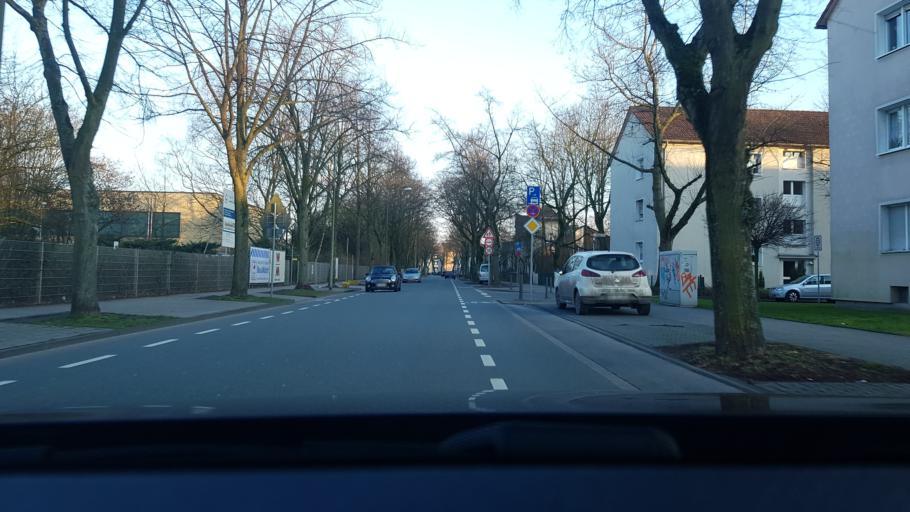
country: DE
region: North Rhine-Westphalia
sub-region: Regierungsbezirk Dusseldorf
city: Hochfeld
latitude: 51.4095
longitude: 6.6959
